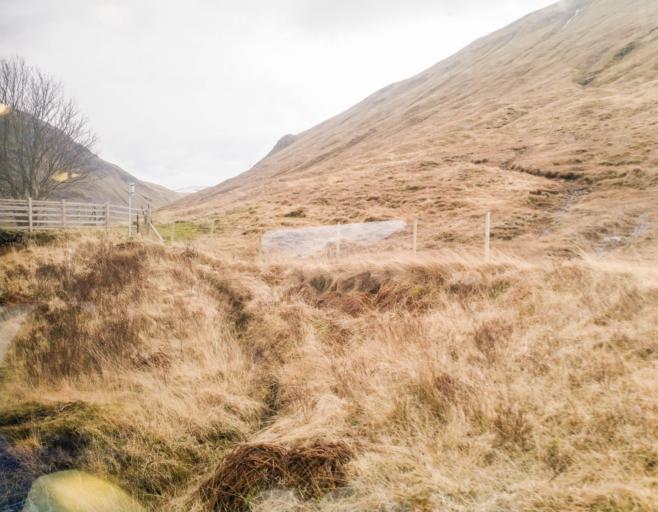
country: GB
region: Scotland
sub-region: Argyll and Bute
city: Garelochhead
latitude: 56.4803
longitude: -4.7115
